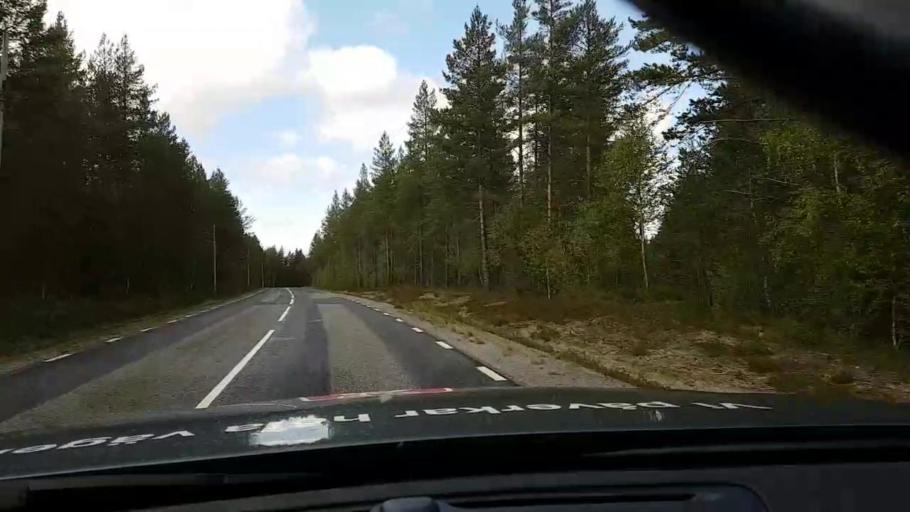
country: SE
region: Vaesterbotten
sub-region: Asele Kommun
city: Asele
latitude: 63.7917
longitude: 17.5826
